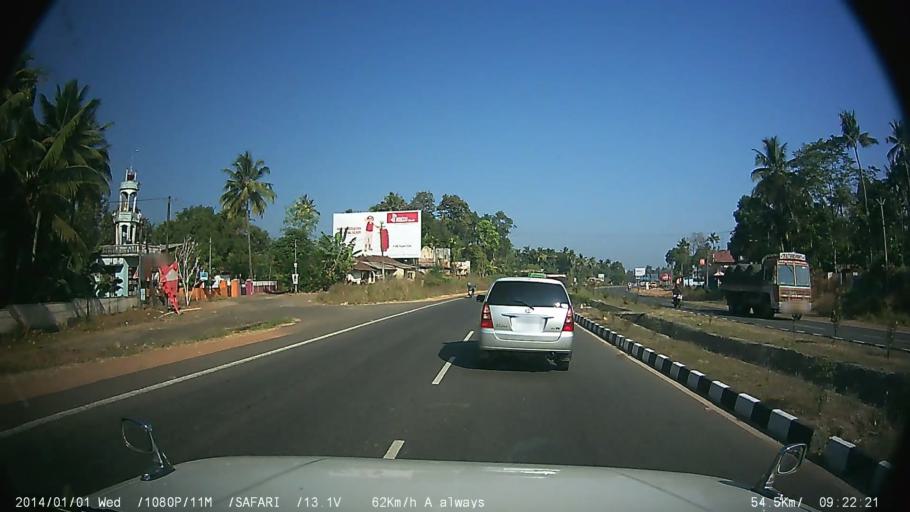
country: IN
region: Kerala
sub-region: Thrissur District
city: Kizhake Chalakudi
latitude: 10.2766
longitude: 76.3444
